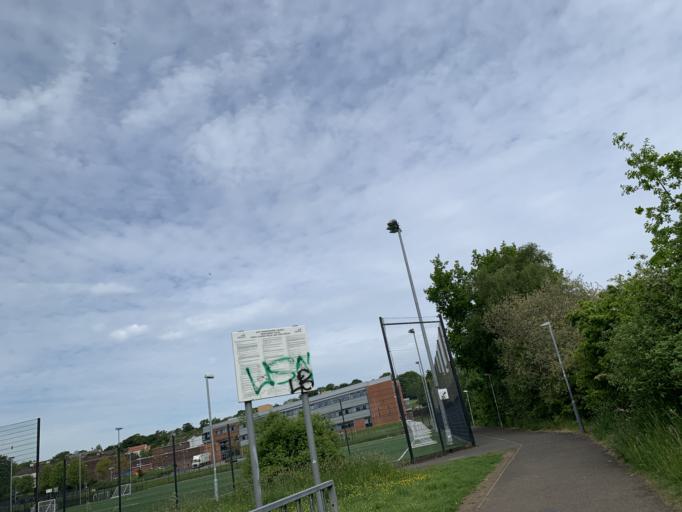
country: GB
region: Scotland
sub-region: East Renfrewshire
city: Giffnock
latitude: 55.8029
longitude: -4.3070
